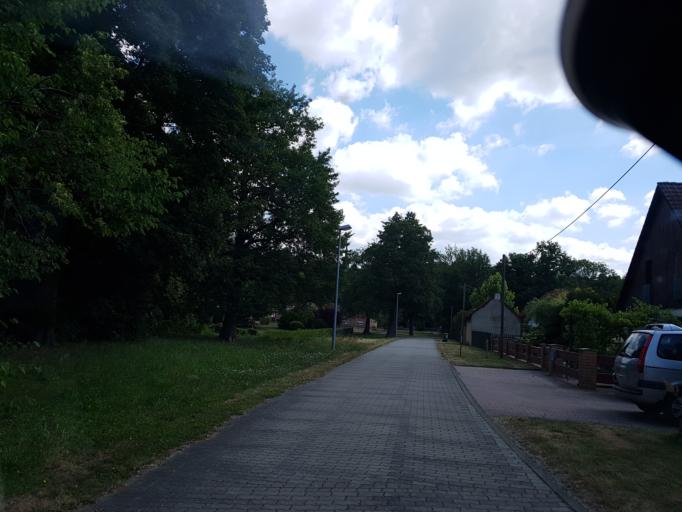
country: DE
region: Brandenburg
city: Altdobern
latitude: 51.6809
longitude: 14.0807
